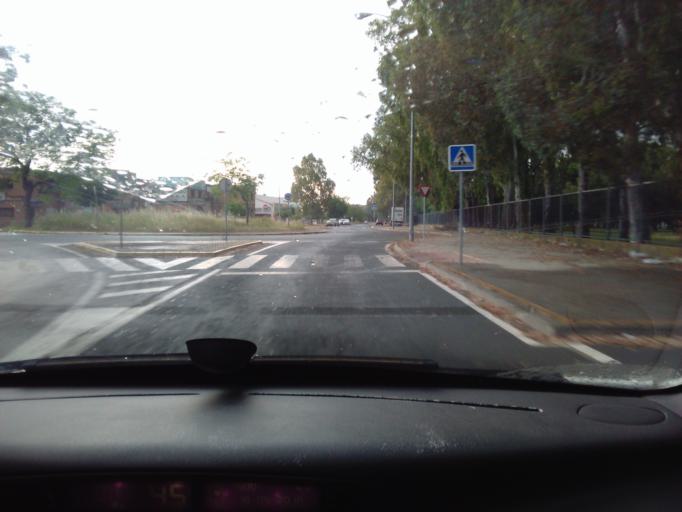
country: ES
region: Andalusia
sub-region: Provincia de Sevilla
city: Sevilla
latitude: 37.3960
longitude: -5.9390
